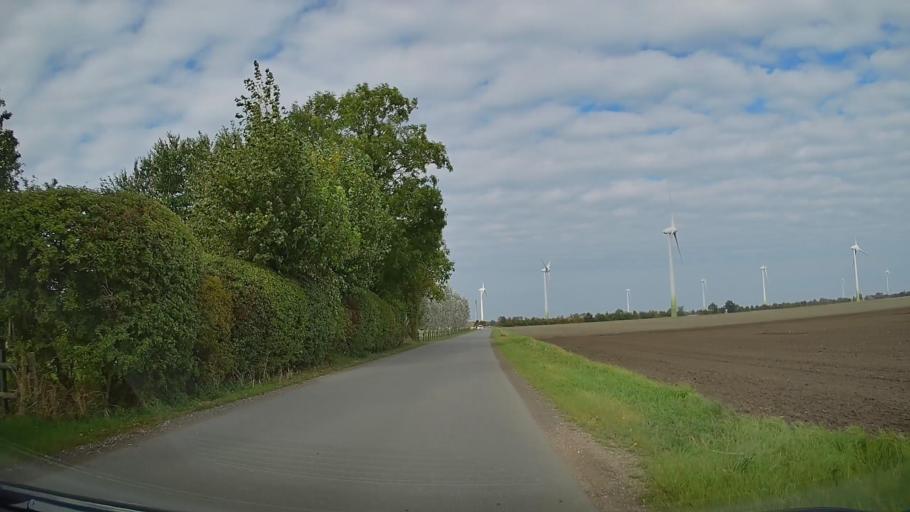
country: DE
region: Schleswig-Holstein
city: Grossenbrode
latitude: 54.5025
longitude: 11.0589
